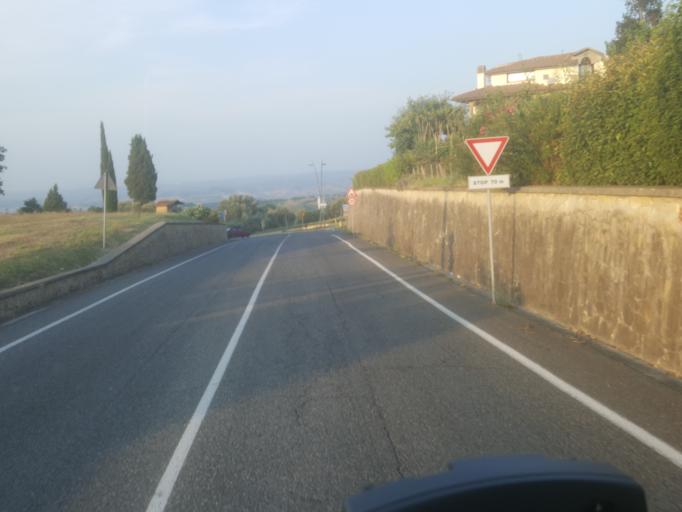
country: IT
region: Tuscany
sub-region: Province of Florence
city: Gambassi Terme
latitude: 43.5416
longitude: 10.9541
